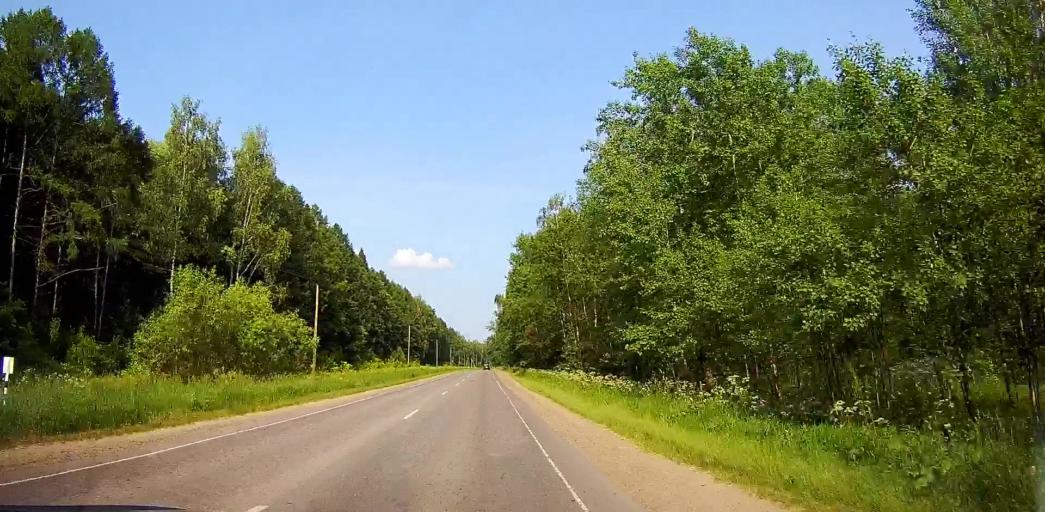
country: RU
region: Moskovskaya
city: Barybino
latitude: 55.2823
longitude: 37.9205
